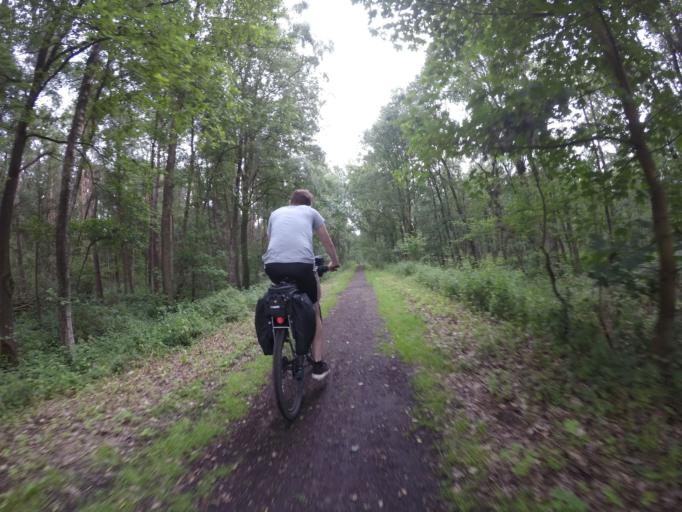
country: DE
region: North Rhine-Westphalia
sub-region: Regierungsbezirk Dusseldorf
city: Schermbeck
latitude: 51.6006
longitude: 6.8550
